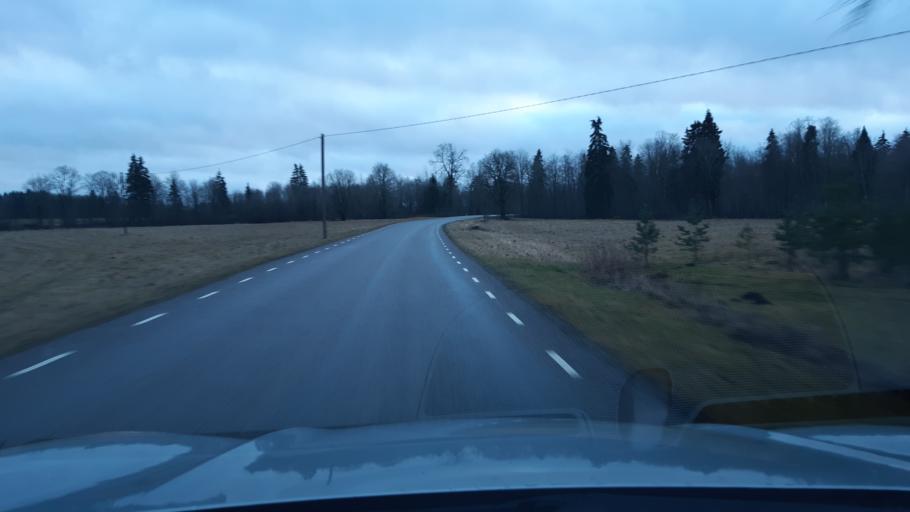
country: EE
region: Raplamaa
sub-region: Kohila vald
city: Kohila
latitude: 59.1056
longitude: 24.6815
